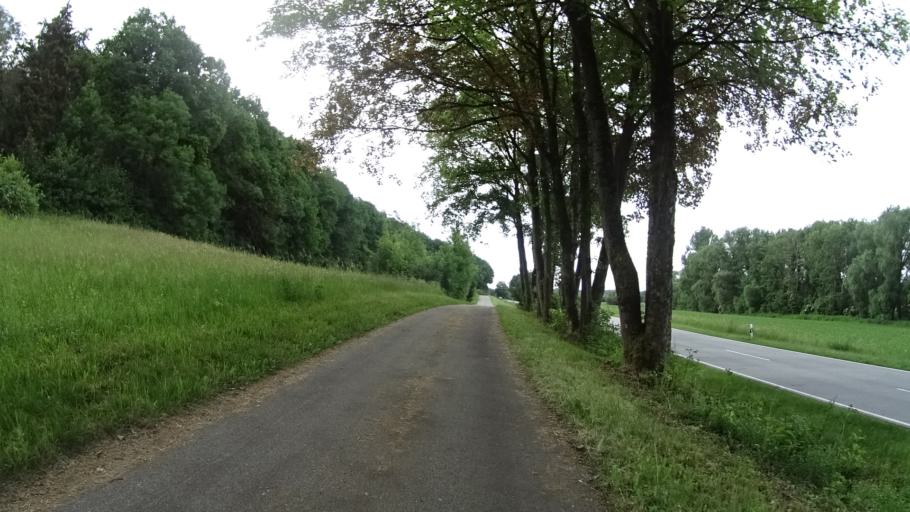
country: DE
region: Bavaria
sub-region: Lower Bavaria
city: Bogen
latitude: 48.8891
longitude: 12.7339
